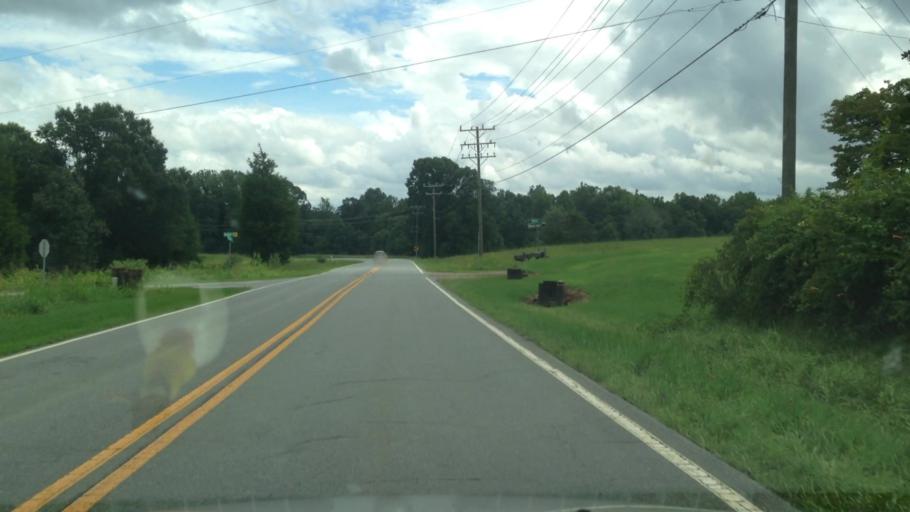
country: US
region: North Carolina
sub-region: Guilford County
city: Oak Ridge
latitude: 36.1949
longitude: -80.0607
